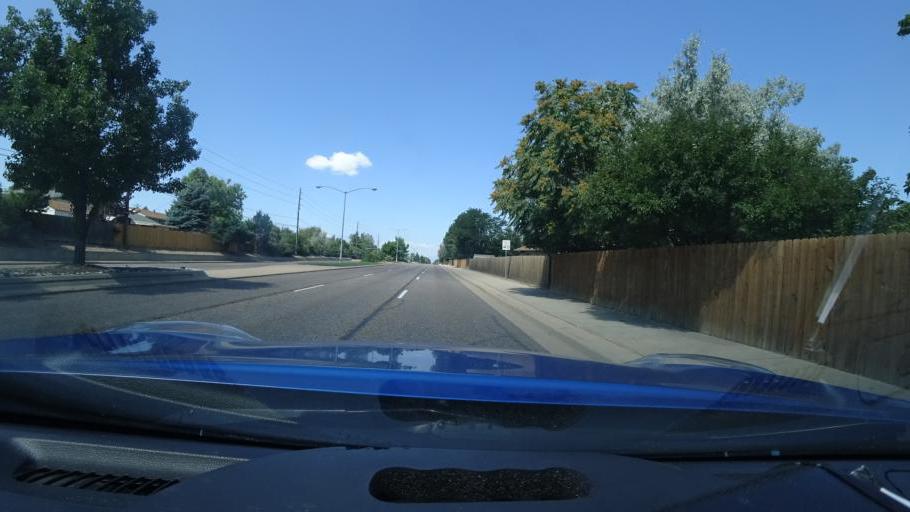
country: US
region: Colorado
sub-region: Adams County
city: Aurora
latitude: 39.7113
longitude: -104.8390
